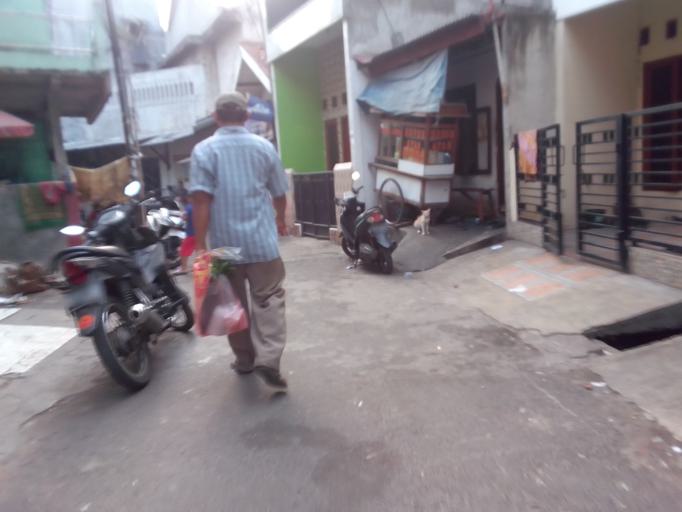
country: ID
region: Jakarta Raya
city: Jakarta
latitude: -6.1938
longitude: 106.8118
